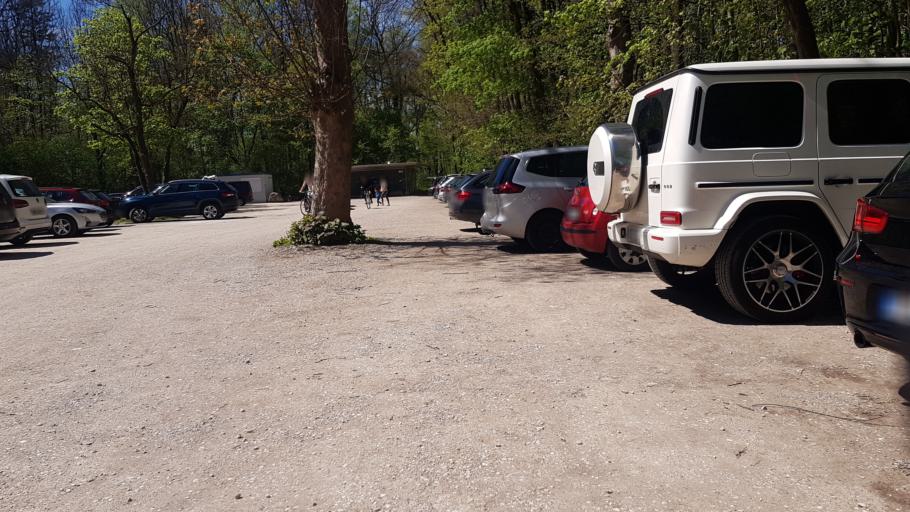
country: DE
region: Bavaria
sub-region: Upper Bavaria
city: Munich
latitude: 48.1016
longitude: 11.5540
